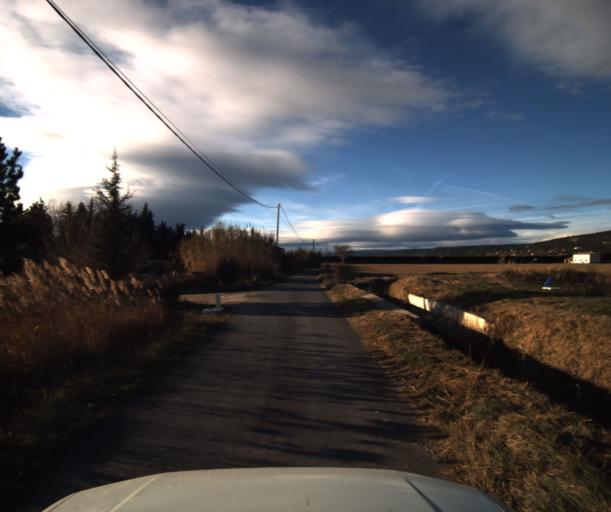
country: FR
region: Provence-Alpes-Cote d'Azur
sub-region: Departement du Vaucluse
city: Villelaure
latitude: 43.6937
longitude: 5.4558
